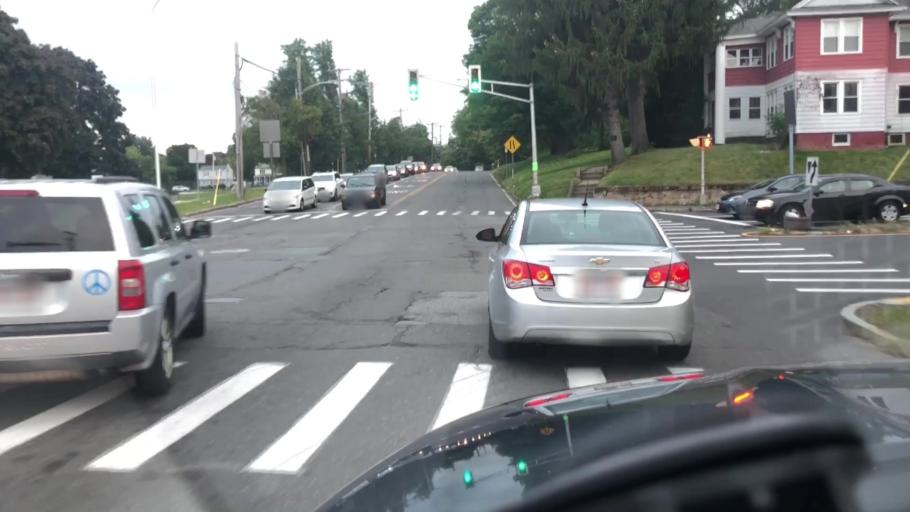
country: US
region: Massachusetts
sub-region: Hampden County
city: Holyoke
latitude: 42.1992
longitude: -72.6312
